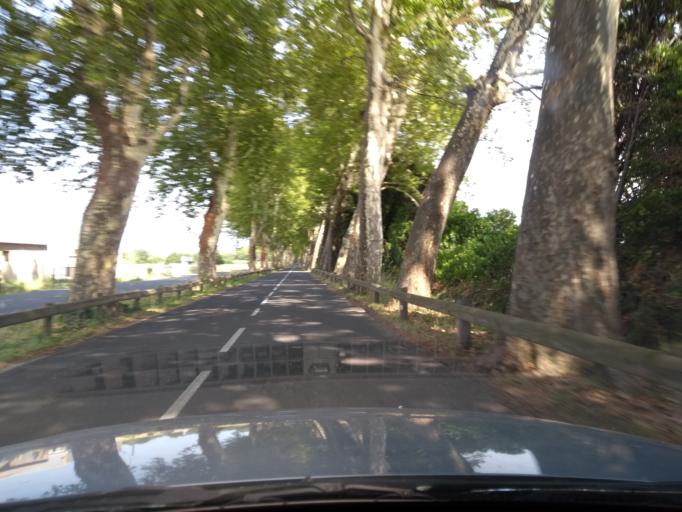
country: FR
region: Languedoc-Roussillon
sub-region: Departement des Pyrenees-Orientales
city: Corneilla-la-Riviere
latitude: 42.6966
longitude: 2.7369
